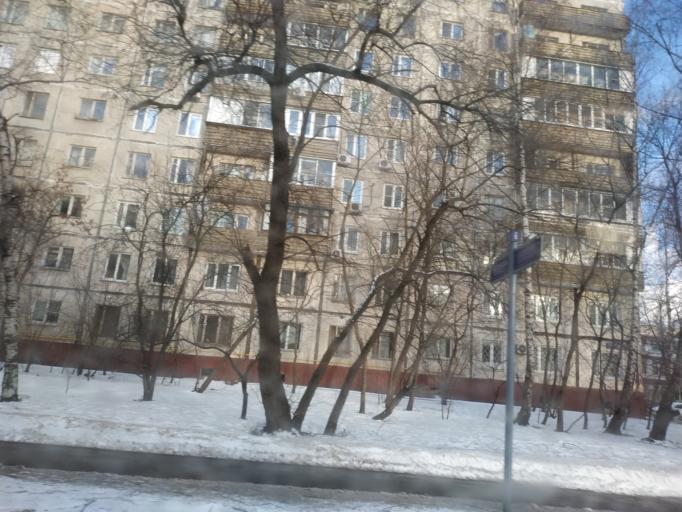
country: RU
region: Moskovskaya
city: Izmaylovo
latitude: 55.7993
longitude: 37.8192
